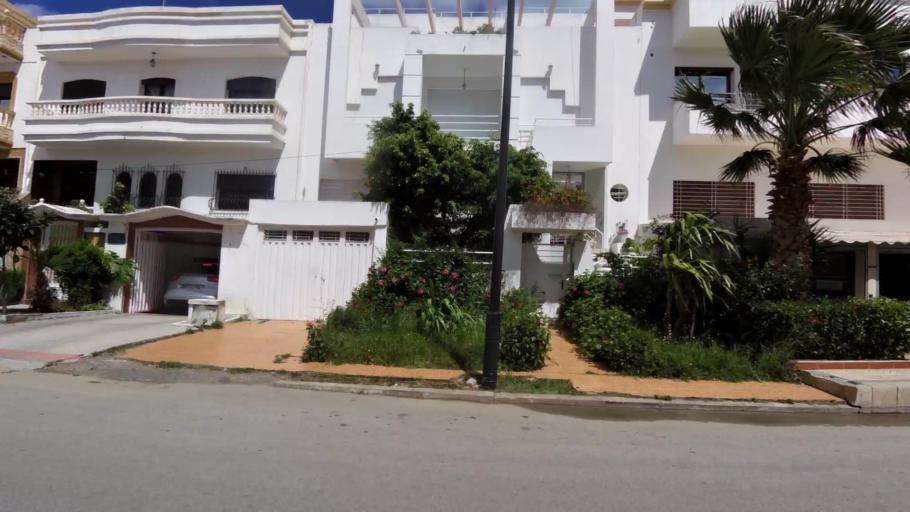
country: MA
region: Tanger-Tetouan
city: Tetouan
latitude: 35.5866
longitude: -5.3346
